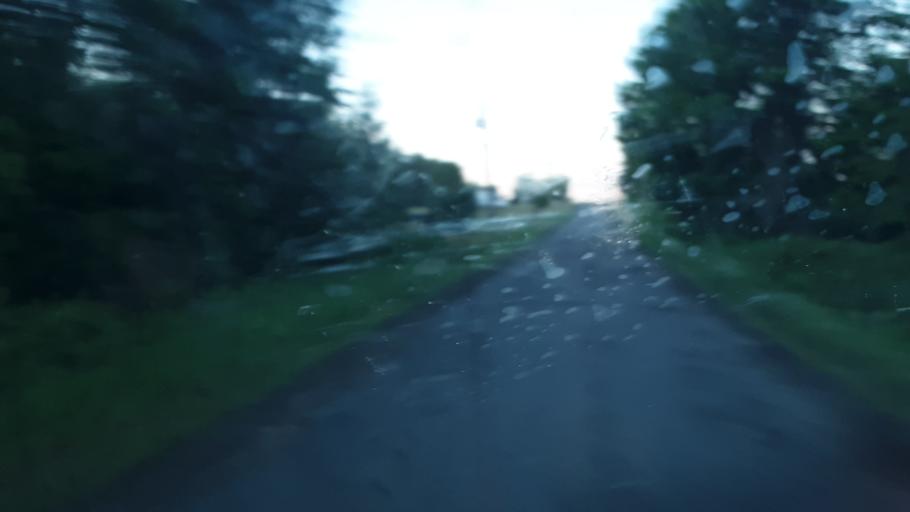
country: US
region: Maine
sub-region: Aroostook County
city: Caribou
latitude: 46.8659
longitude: -68.1374
